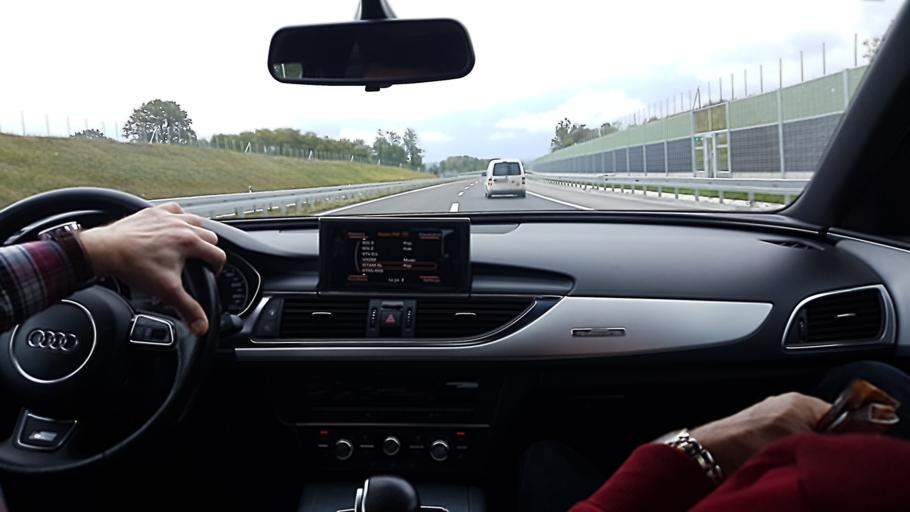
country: BA
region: Republika Srpska
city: Prnjavor
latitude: 44.8473
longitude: 17.7642
